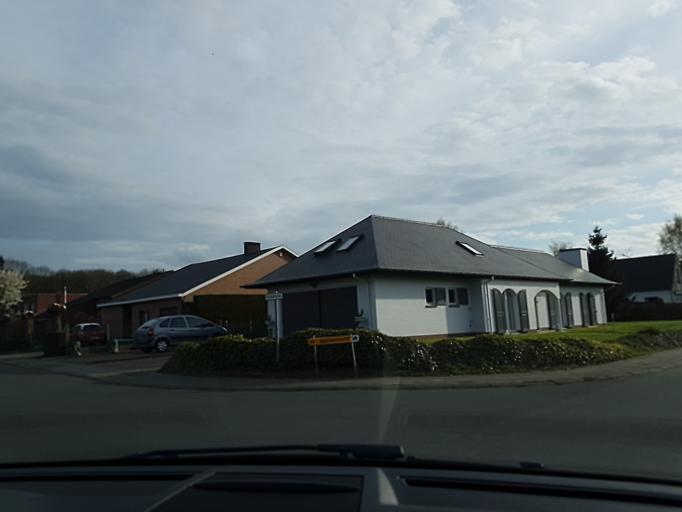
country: BE
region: Flanders
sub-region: Provincie West-Vlaanderen
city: Zedelgem
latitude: 51.1311
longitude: 3.1736
